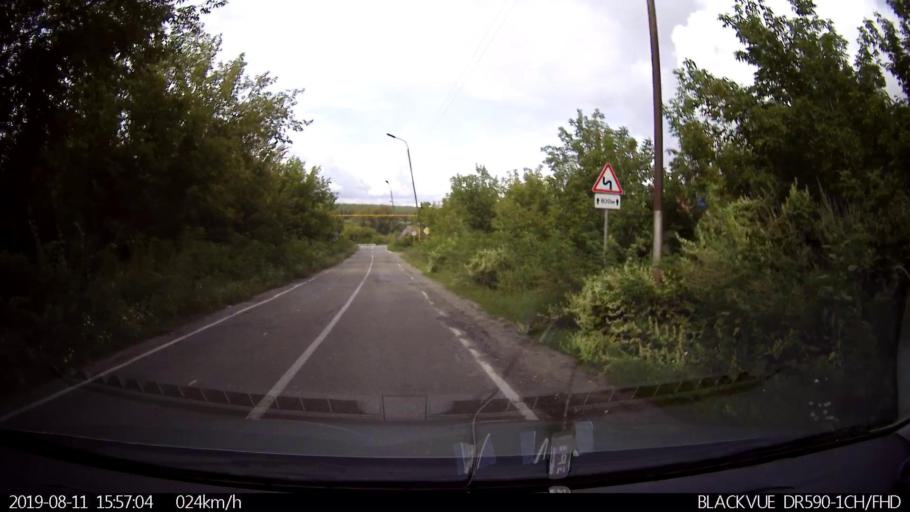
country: RU
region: Ulyanovsk
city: Ignatovka
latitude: 53.9494
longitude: 47.6525
